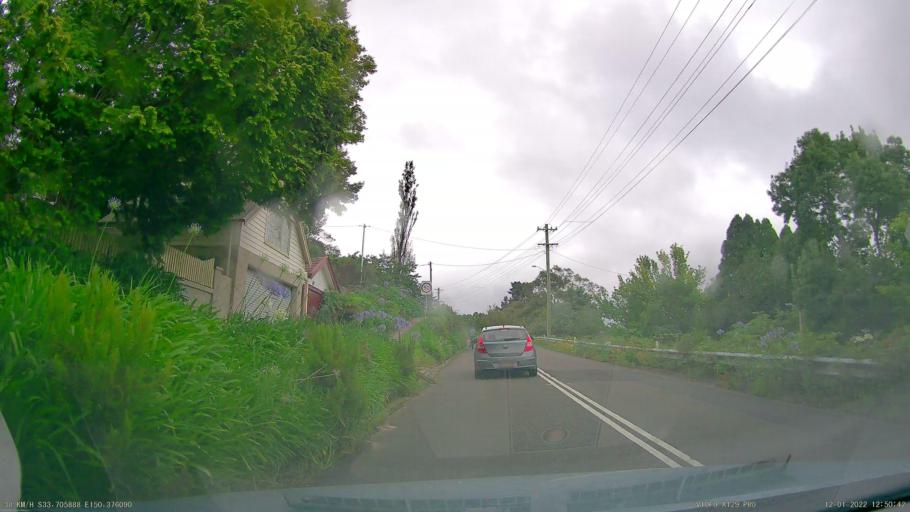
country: AU
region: New South Wales
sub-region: Blue Mountains Municipality
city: Leura
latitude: -33.7057
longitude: 150.3761
